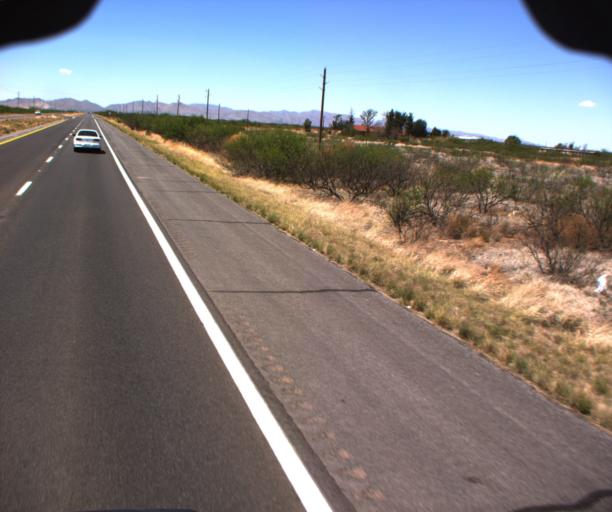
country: US
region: Arizona
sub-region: Cochise County
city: Pirtleville
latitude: 31.3587
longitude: -109.6445
